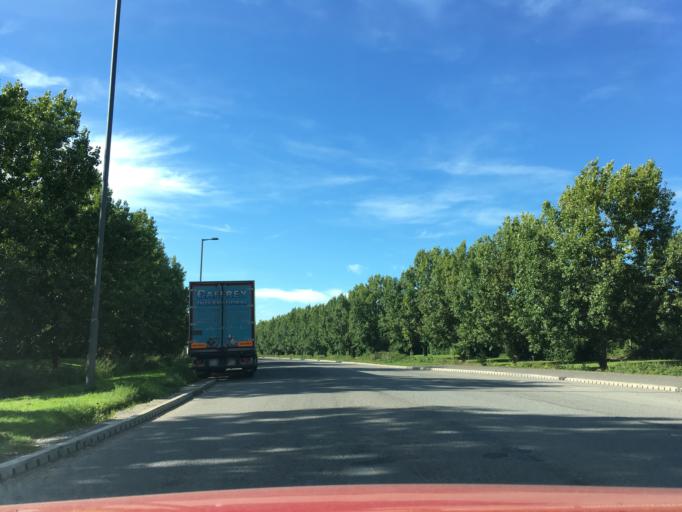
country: GB
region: England
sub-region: South Gloucestershire
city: Severn Beach
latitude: 51.5490
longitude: -2.6468
